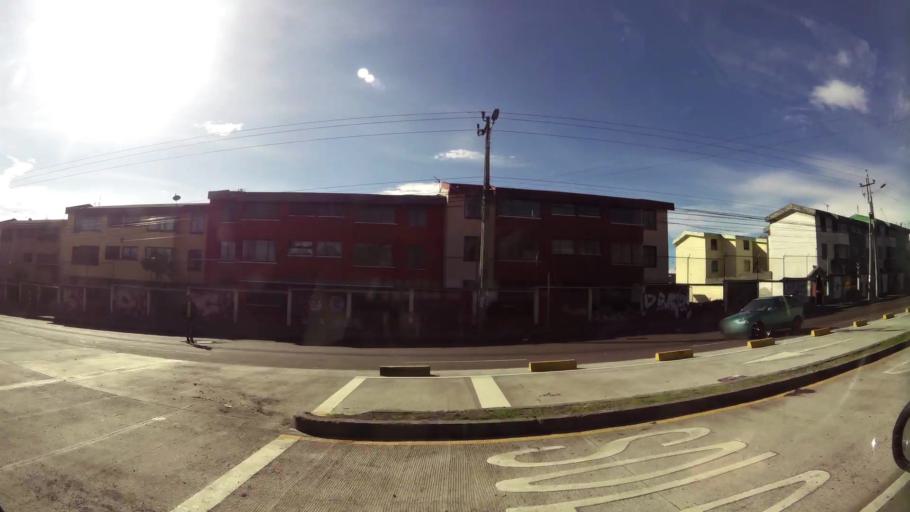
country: EC
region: Pichincha
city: Quito
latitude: -0.3134
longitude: -78.5482
